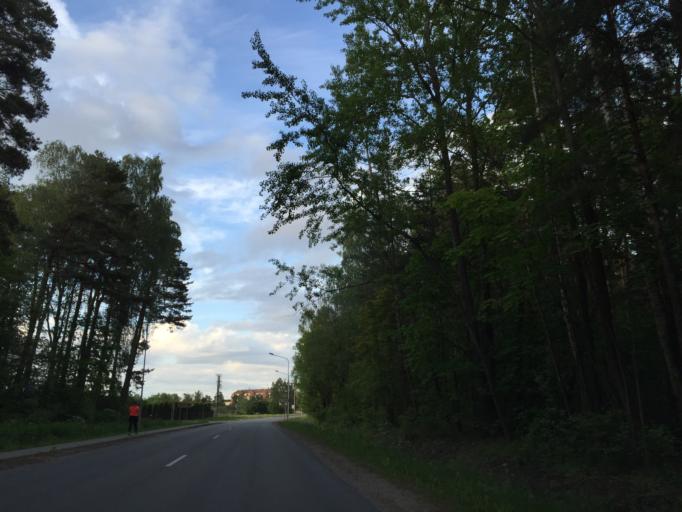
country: LV
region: Babite
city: Pinki
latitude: 56.9395
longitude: 23.8972
